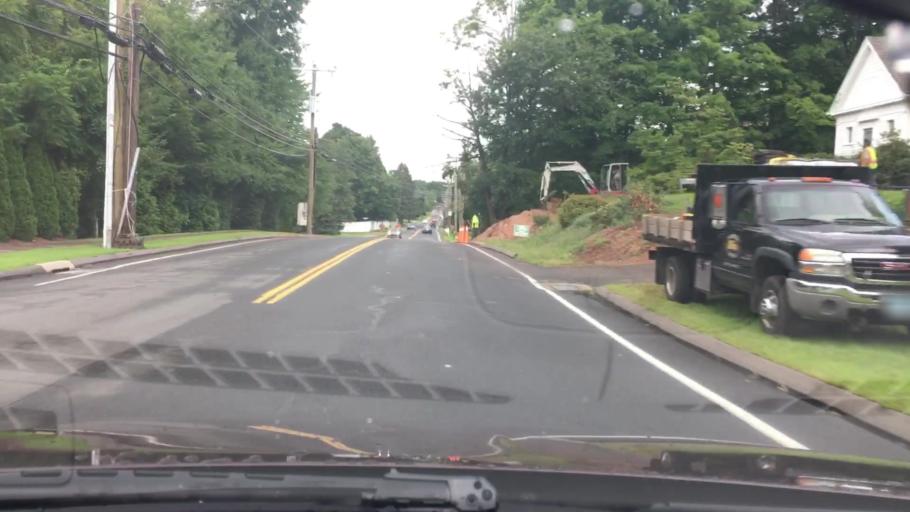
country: US
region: Connecticut
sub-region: Hartford County
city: Manchester
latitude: 41.7512
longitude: -72.5401
